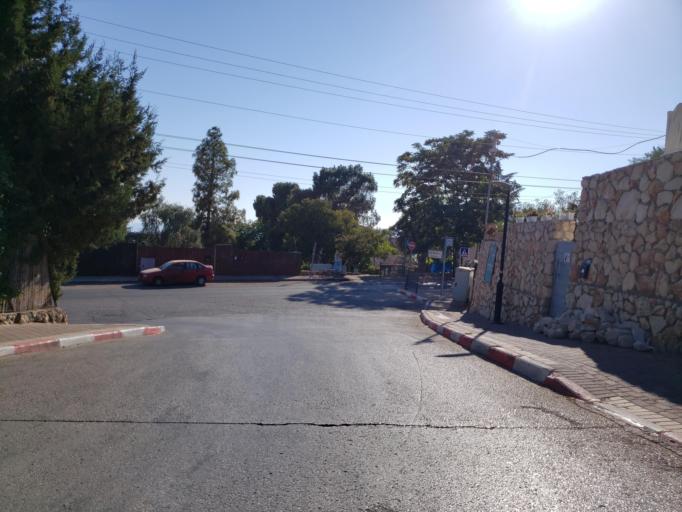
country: IL
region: Northern District
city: Safed
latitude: 32.9602
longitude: 35.4963
